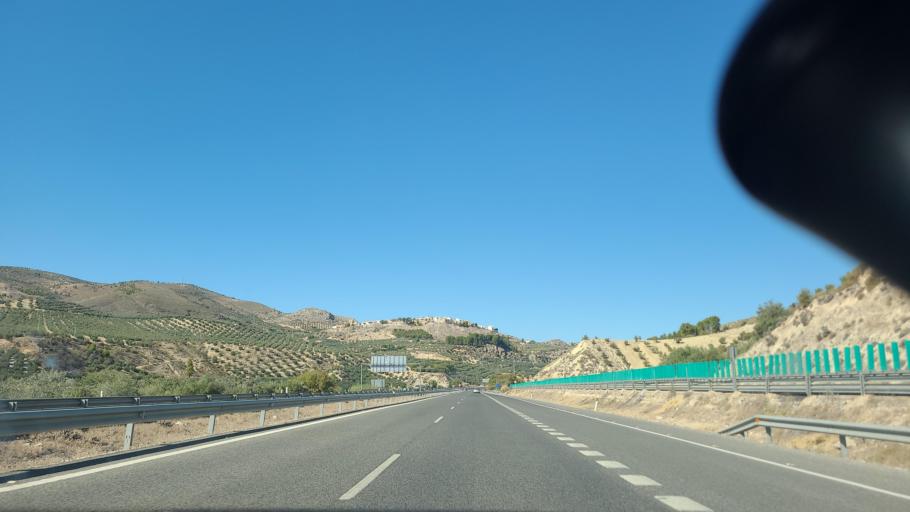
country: ES
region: Andalusia
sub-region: Provincia de Jaen
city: La Guardia de Jaen
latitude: 37.7289
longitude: -3.6818
